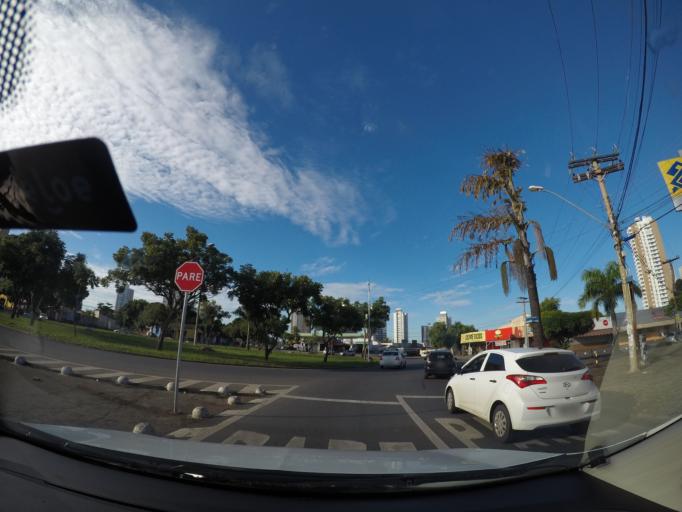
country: BR
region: Goias
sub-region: Goiania
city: Goiania
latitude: -16.7320
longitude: -49.2722
